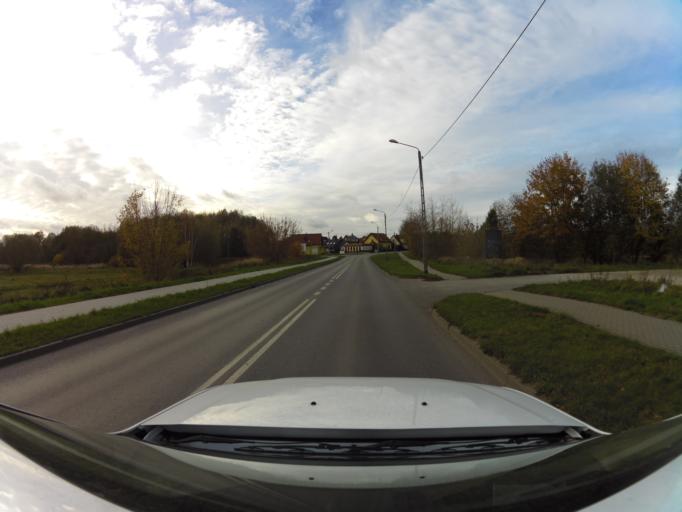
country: PL
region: West Pomeranian Voivodeship
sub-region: Powiat gryficki
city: Gryfice
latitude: 53.9201
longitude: 15.1896
